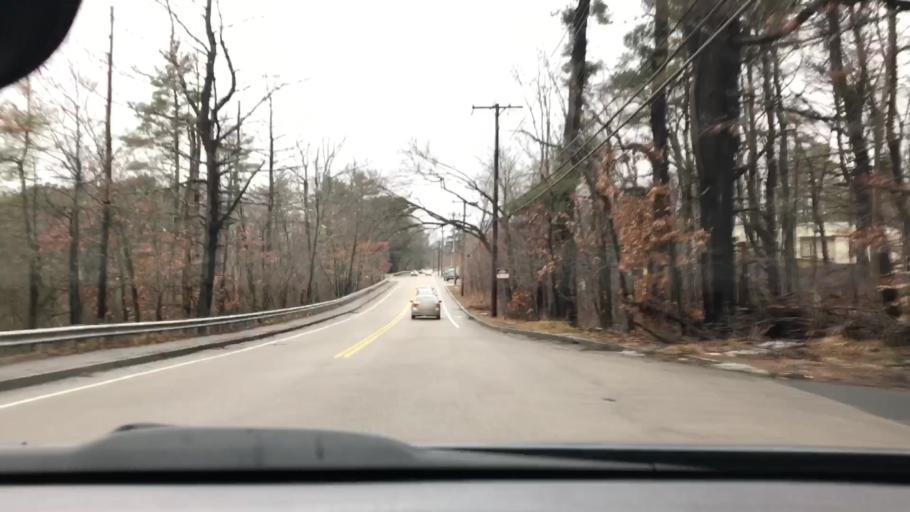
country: US
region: Massachusetts
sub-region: Middlesex County
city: Cochituate
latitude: 42.3118
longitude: -71.3351
